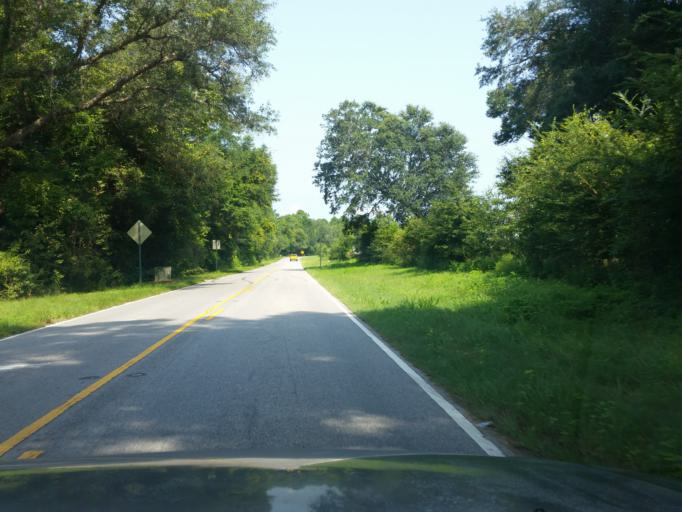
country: US
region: Florida
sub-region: Escambia County
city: Bellview
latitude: 30.4628
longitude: -87.3469
